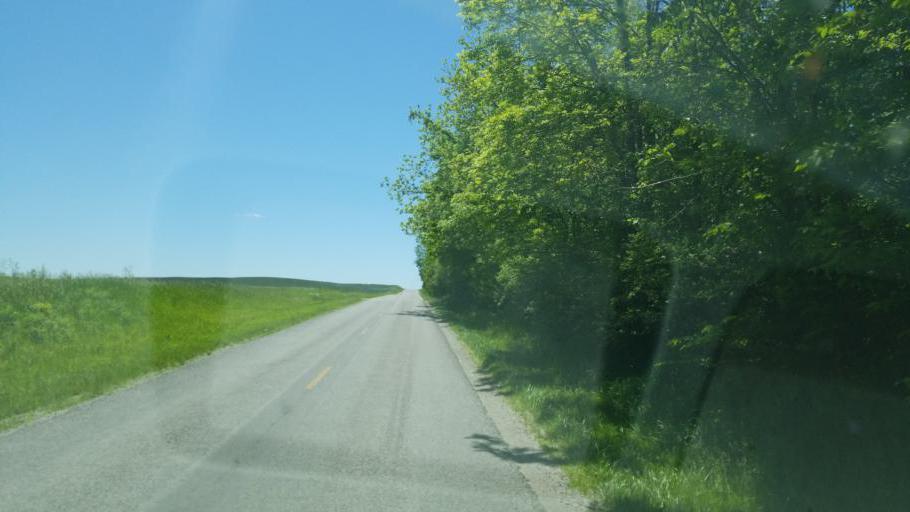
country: US
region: Ohio
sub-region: Mercer County
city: Fort Recovery
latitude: 40.3209
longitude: -84.8035
